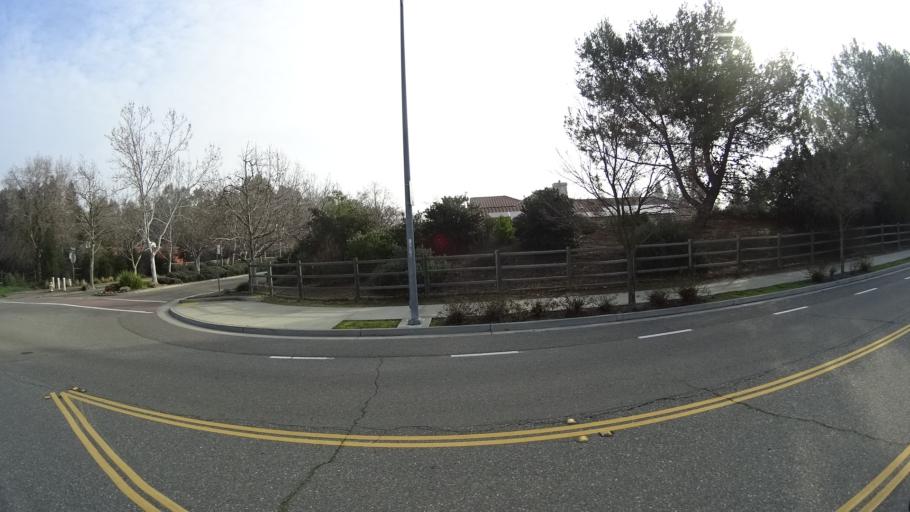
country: US
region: California
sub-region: Yolo County
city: Davis
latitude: 38.5700
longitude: -121.7672
